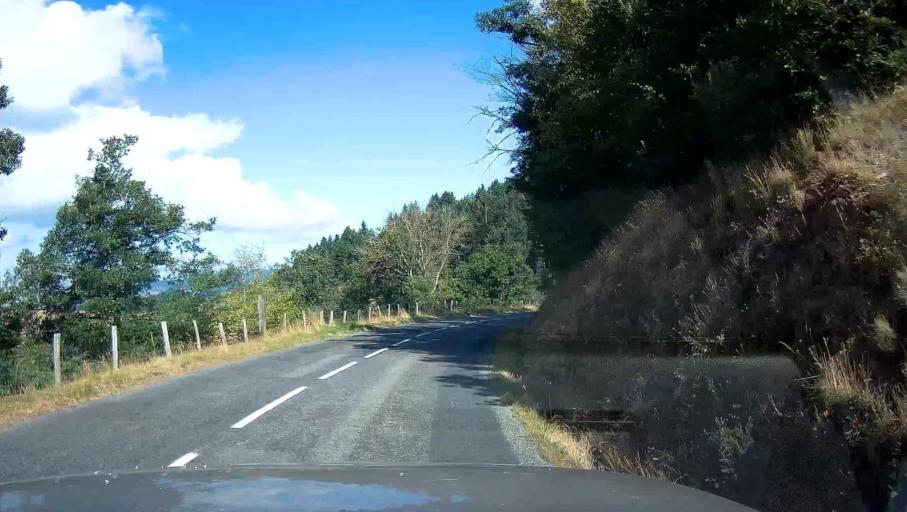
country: FR
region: Rhone-Alpes
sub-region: Departement du Rhone
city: Grandris
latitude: 46.0024
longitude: 4.5420
